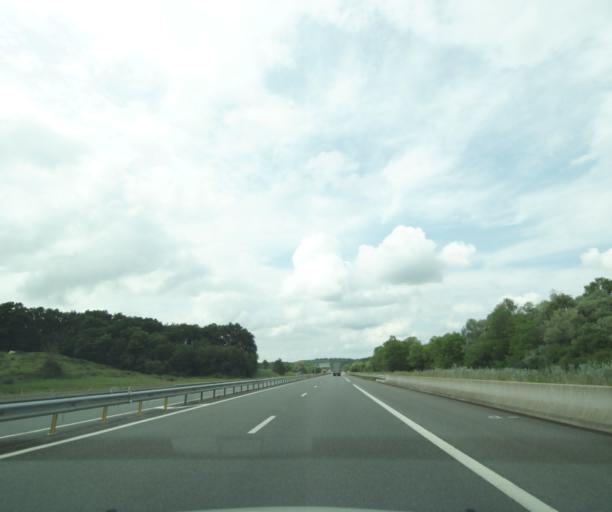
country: FR
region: Centre
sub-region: Departement du Cher
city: Orval
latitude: 46.7324
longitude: 2.4294
